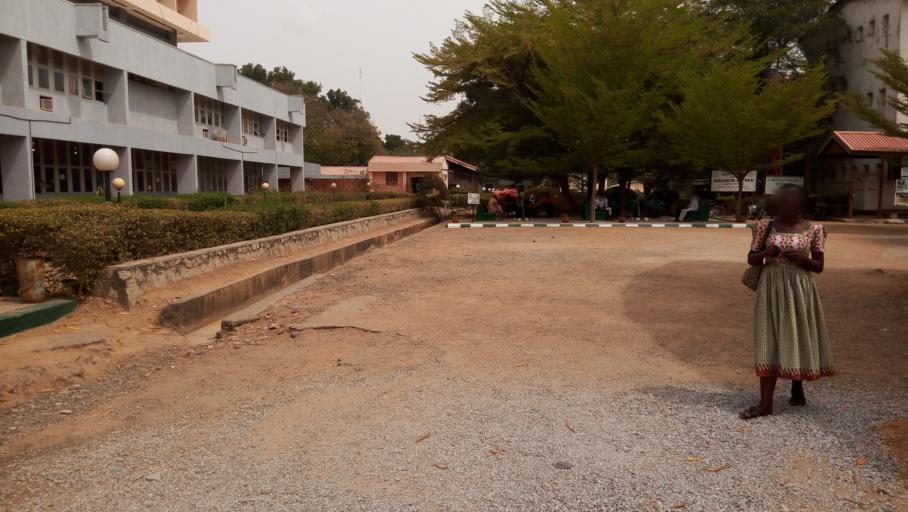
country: NG
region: Kaduna
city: Zaria
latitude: 11.1506
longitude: 7.6542
